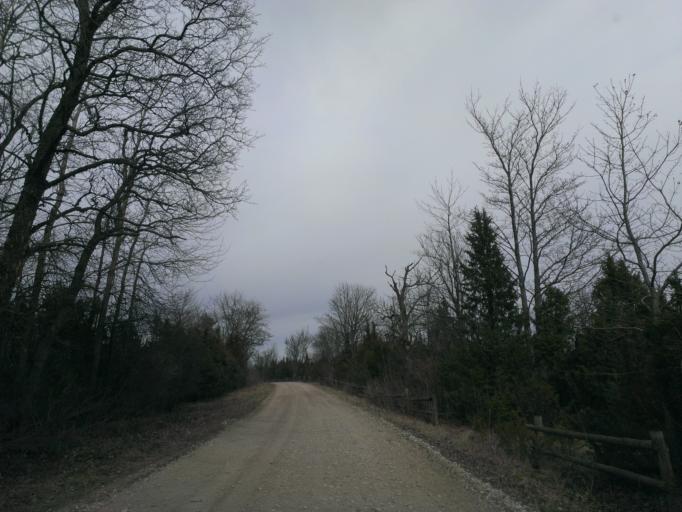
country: EE
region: Laeaene
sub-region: Lihula vald
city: Lihula
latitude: 58.5698
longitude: 23.5479
